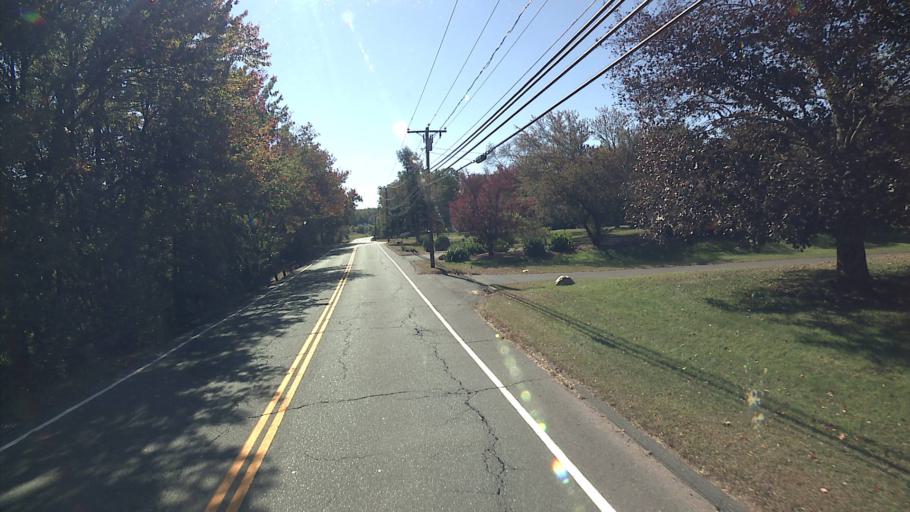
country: US
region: Connecticut
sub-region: Tolland County
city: Somers
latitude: 41.9770
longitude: -72.4452
